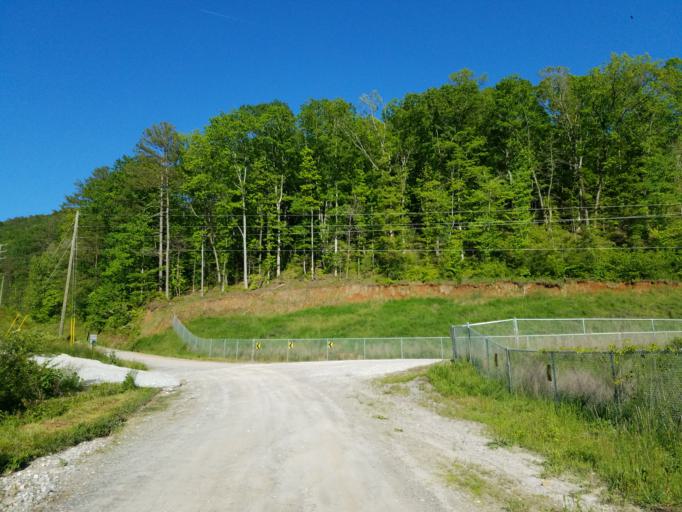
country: US
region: Georgia
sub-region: Gilmer County
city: Ellijay
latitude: 34.6043
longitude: -84.5082
